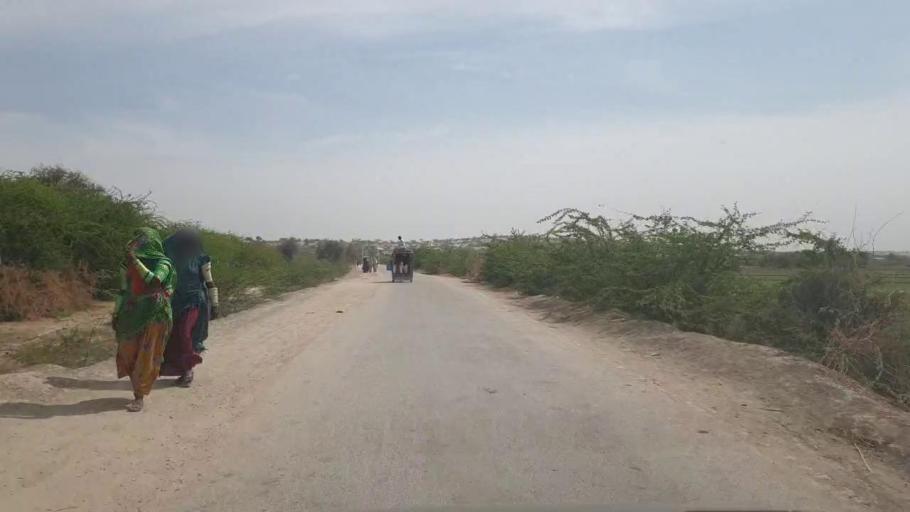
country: PK
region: Sindh
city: Umarkot
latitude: 25.2261
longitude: 69.7112
